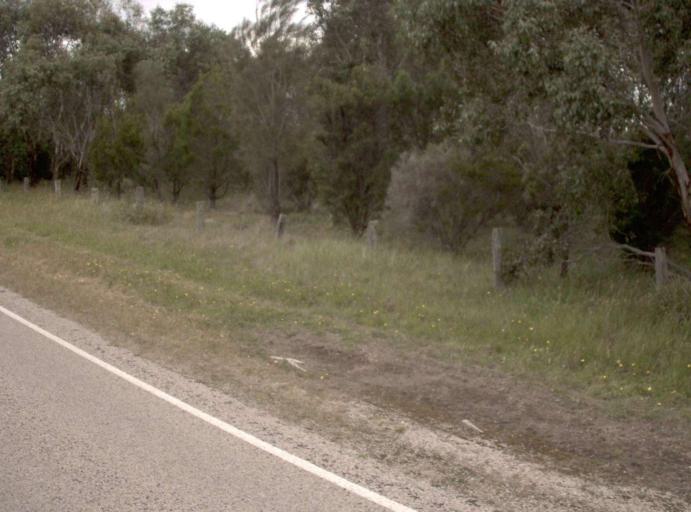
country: AU
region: Victoria
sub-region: East Gippsland
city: Bairnsdale
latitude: -37.9024
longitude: 147.5523
